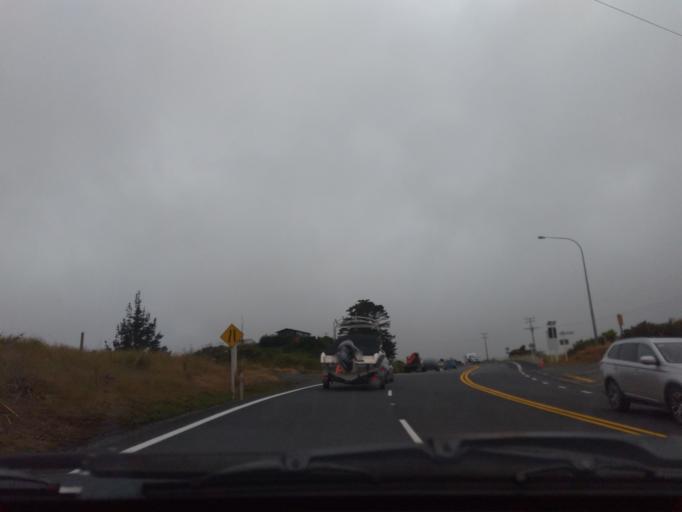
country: NZ
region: Northland
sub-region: Whangarei
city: Ruakaka
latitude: -36.0683
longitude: 174.4215
